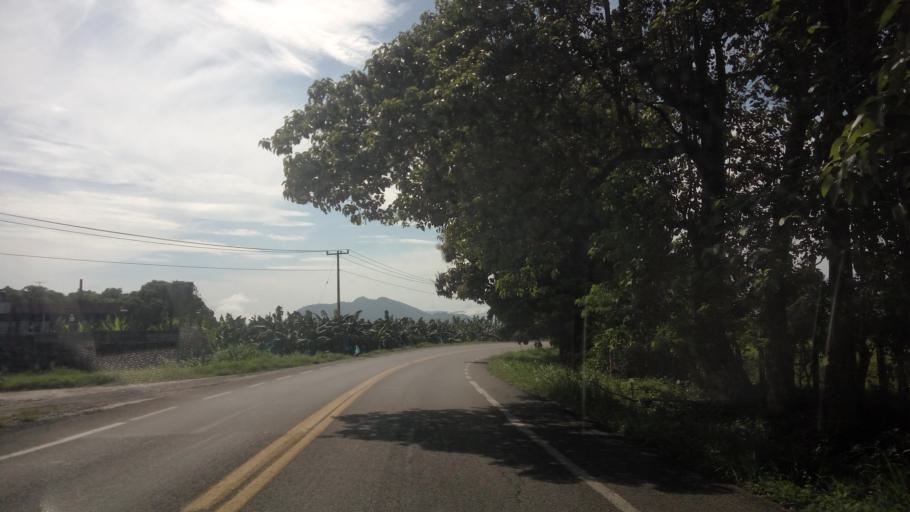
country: MX
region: Tabasco
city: Teapa
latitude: 17.6012
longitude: -92.9636
